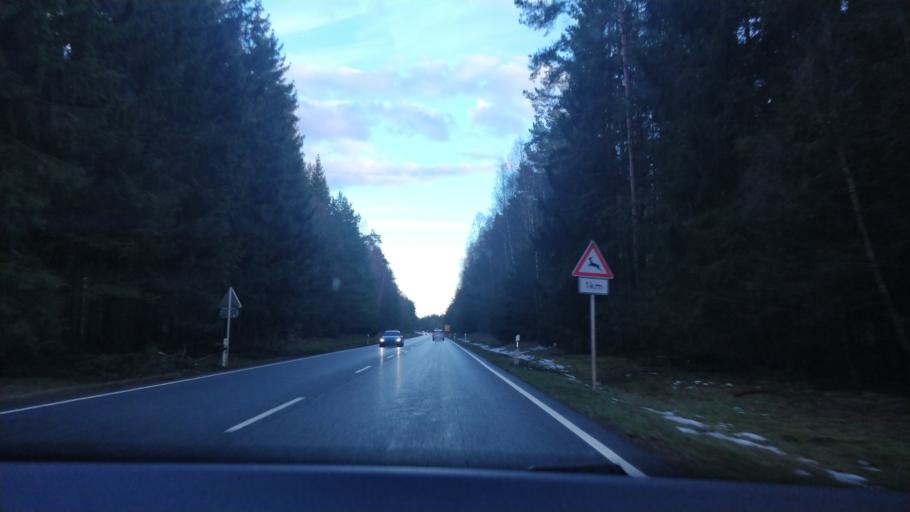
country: DE
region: Bavaria
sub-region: Upper Palatinate
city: Schwarzenbach
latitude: 49.7295
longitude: 11.9616
